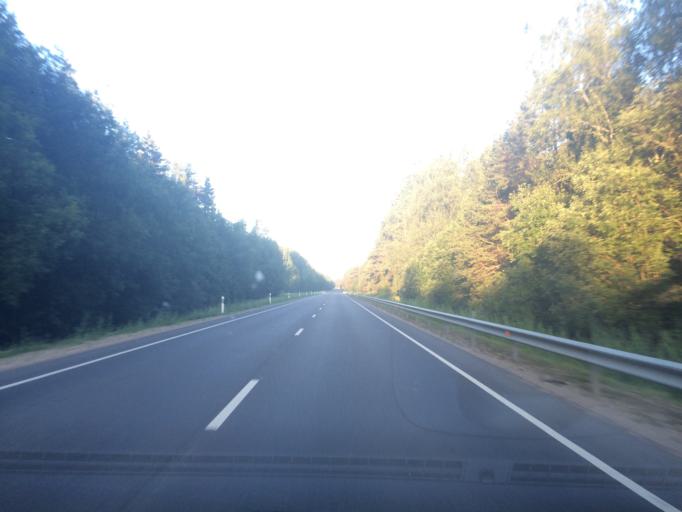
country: LT
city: Zarasai
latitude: 55.6856
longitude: 26.1285
